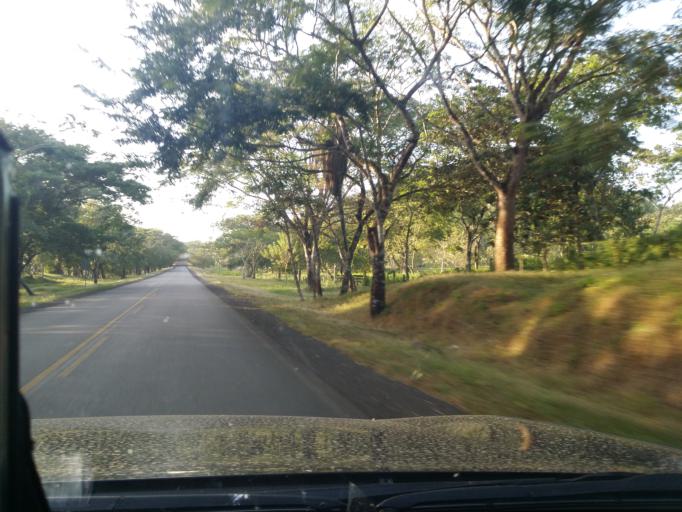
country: NI
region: Rio San Juan
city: San Miguelito
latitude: 11.3986
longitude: -84.8233
